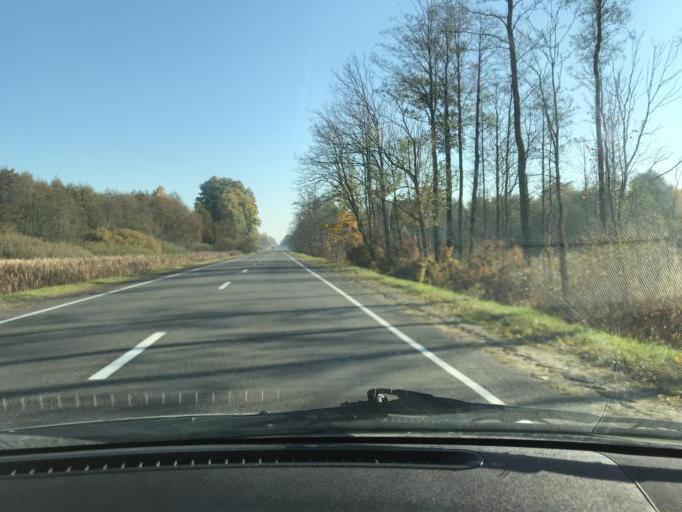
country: BY
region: Brest
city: Lyakhavichy
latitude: 52.9578
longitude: 26.3386
